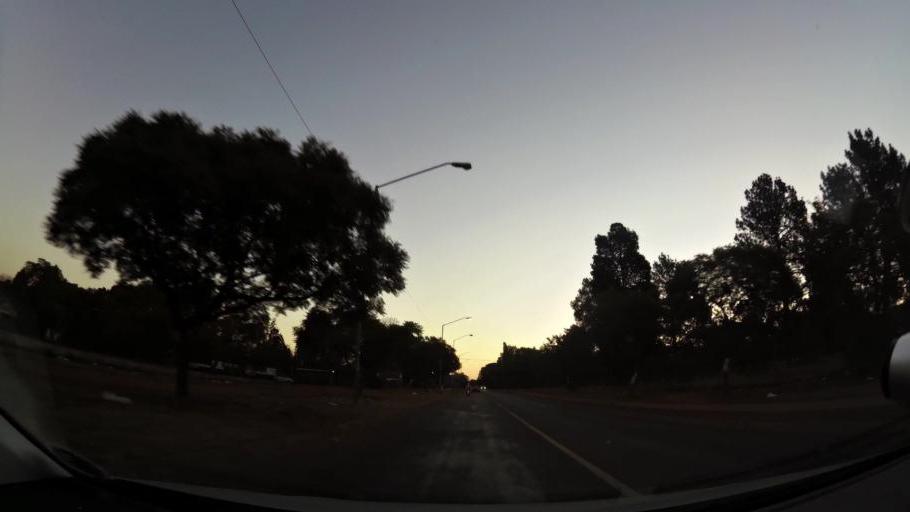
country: ZA
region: Gauteng
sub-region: City of Tshwane Metropolitan Municipality
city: Pretoria
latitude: -25.7390
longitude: 28.1571
